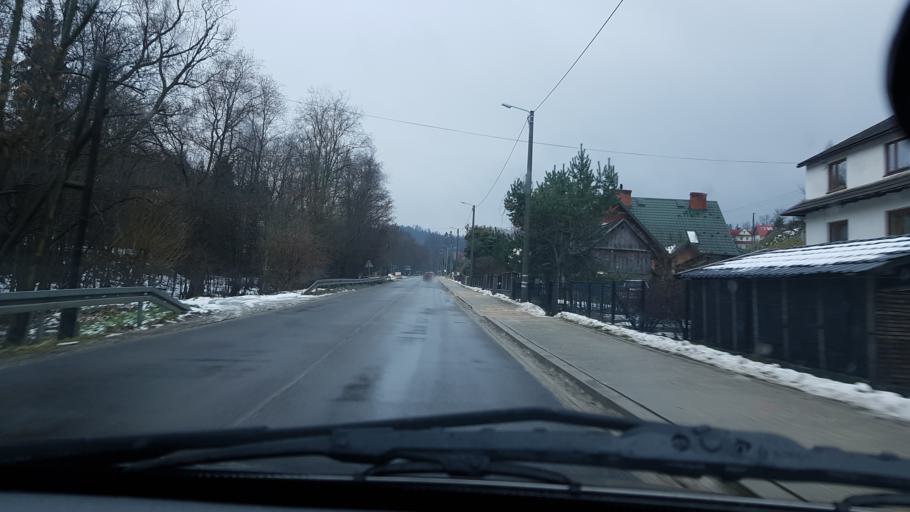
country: PL
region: Lesser Poland Voivodeship
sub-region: Powiat nowotarski
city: Raba Wyzna
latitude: 49.5412
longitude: 19.8919
